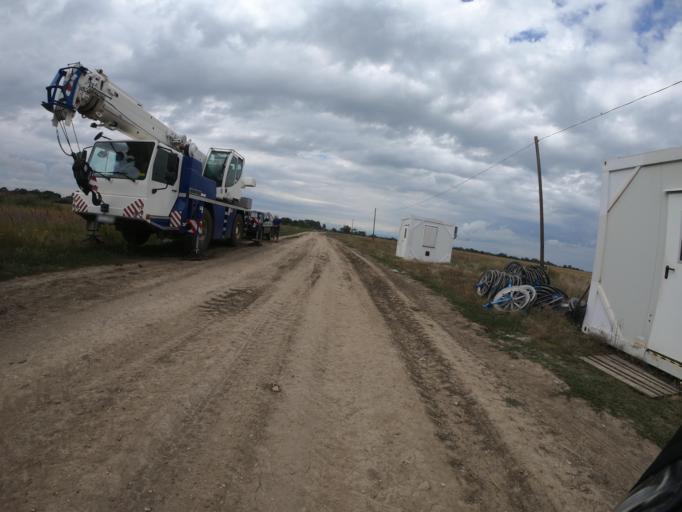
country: HU
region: Jasz-Nagykun-Szolnok
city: Tiszafured
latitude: 47.7106
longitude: 20.8120
